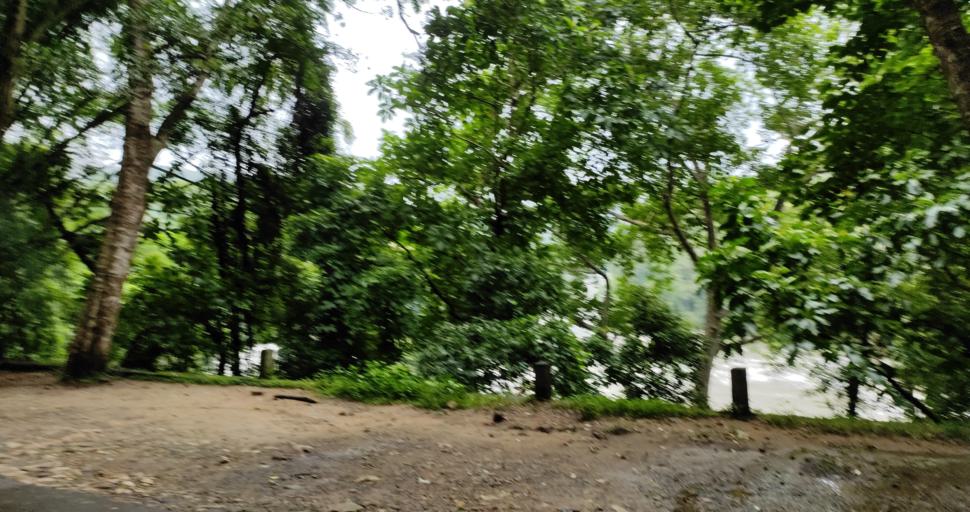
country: IN
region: Kerala
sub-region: Ernakulam
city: Angamali
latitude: 10.2925
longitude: 76.5656
